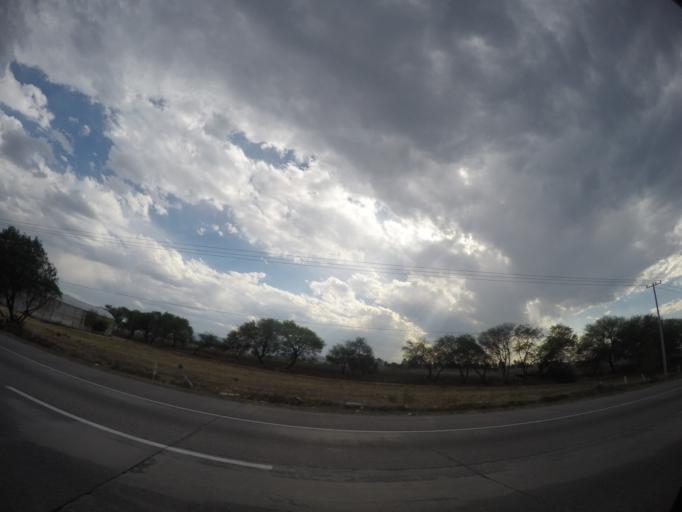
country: MX
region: Queretaro
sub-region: San Juan del Rio
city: Paso de Mata
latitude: 20.3224
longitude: -99.9343
